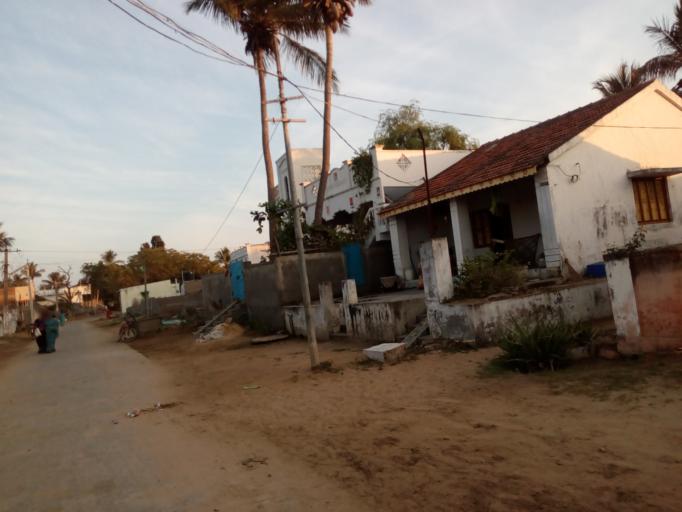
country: IN
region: Andhra Pradesh
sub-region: Prakasam
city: Vetapalem
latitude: 15.7251
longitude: 80.2556
